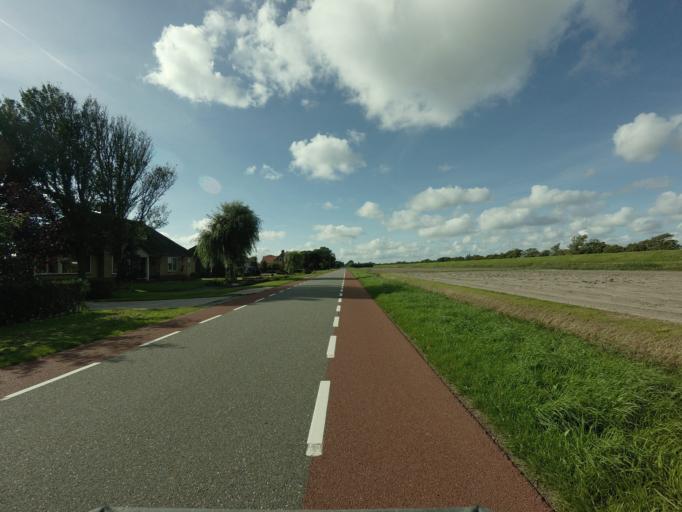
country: NL
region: North Holland
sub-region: Gemeente Den Helder
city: Den Helder
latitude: 52.9019
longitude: 4.8259
